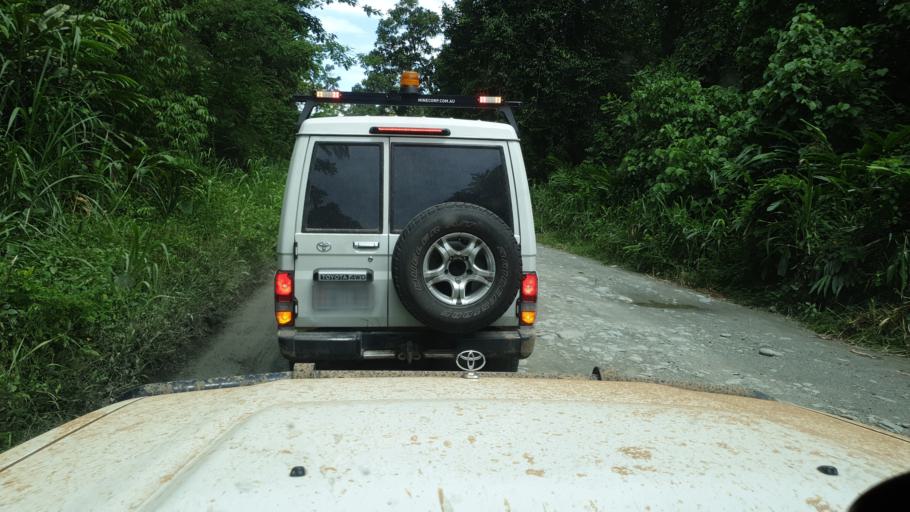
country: PG
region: Northern Province
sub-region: Sohe
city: Kokoda
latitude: -8.9162
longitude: 147.9189
